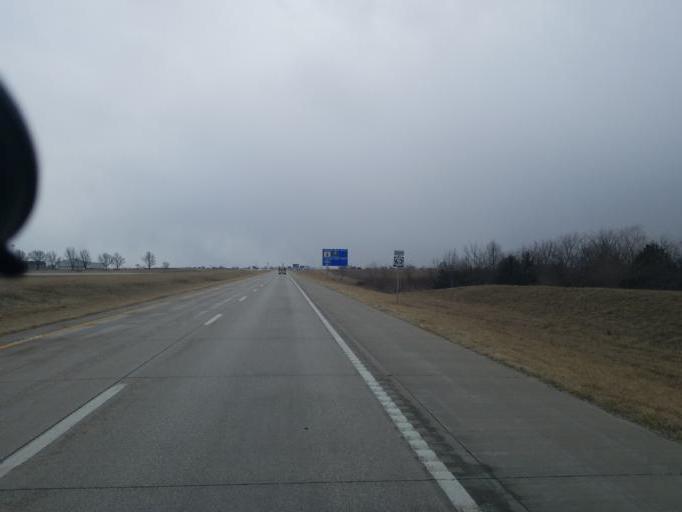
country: US
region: Missouri
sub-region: Randolph County
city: Moberly
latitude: 39.4680
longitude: -92.4350
